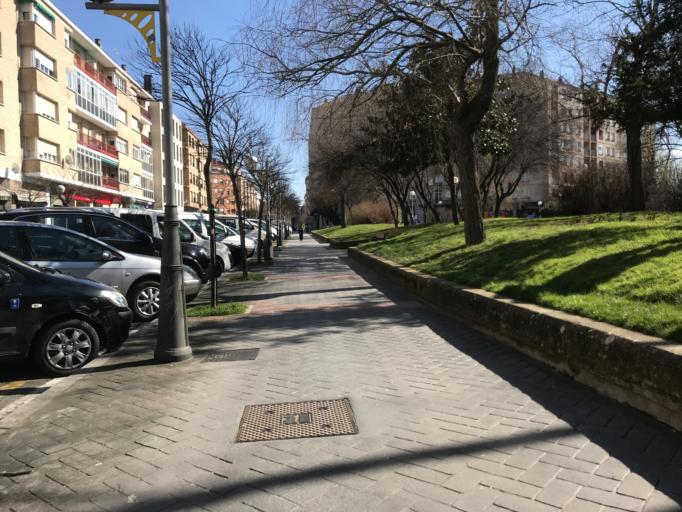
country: ES
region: Basque Country
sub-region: Provincia de Alava
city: Gasteiz / Vitoria
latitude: 42.8395
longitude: -2.6675
